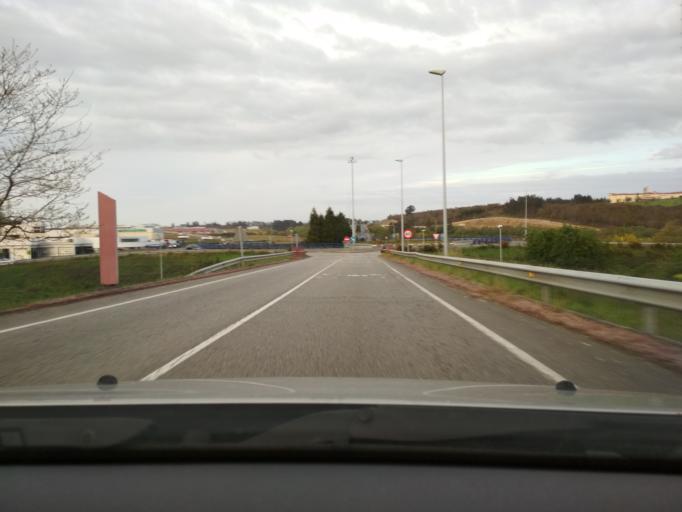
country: ES
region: Galicia
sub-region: Provincia da Coruna
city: Santiago de Compostela
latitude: 42.8984
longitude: -8.5117
